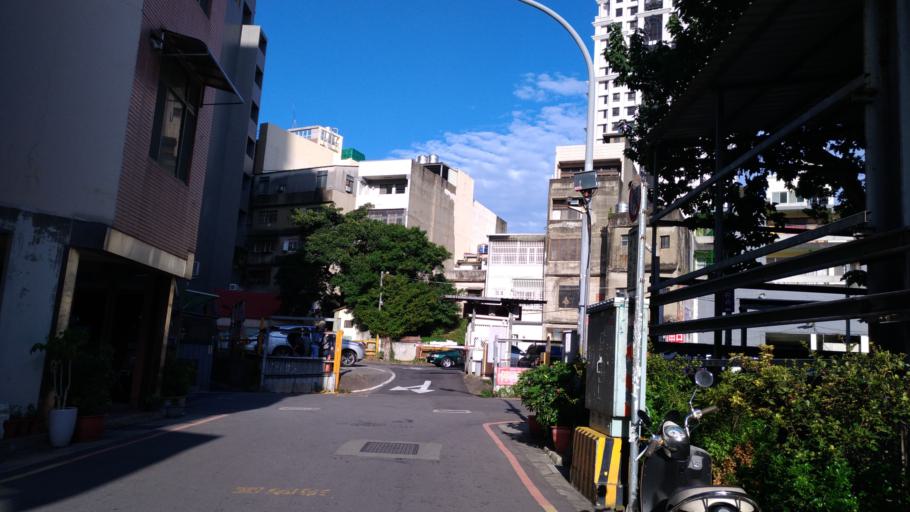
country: TW
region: Taiwan
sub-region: Hsinchu
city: Hsinchu
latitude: 24.8054
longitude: 120.9647
